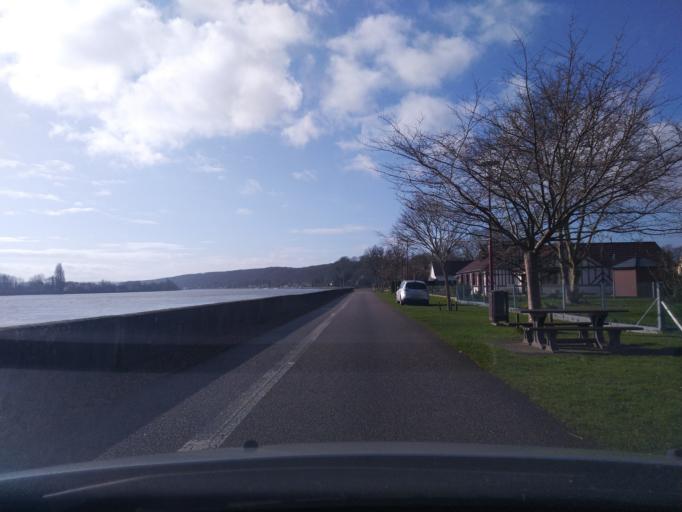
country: FR
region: Haute-Normandie
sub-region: Departement de la Seine-Maritime
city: Duclair
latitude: 49.4713
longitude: 0.8625
